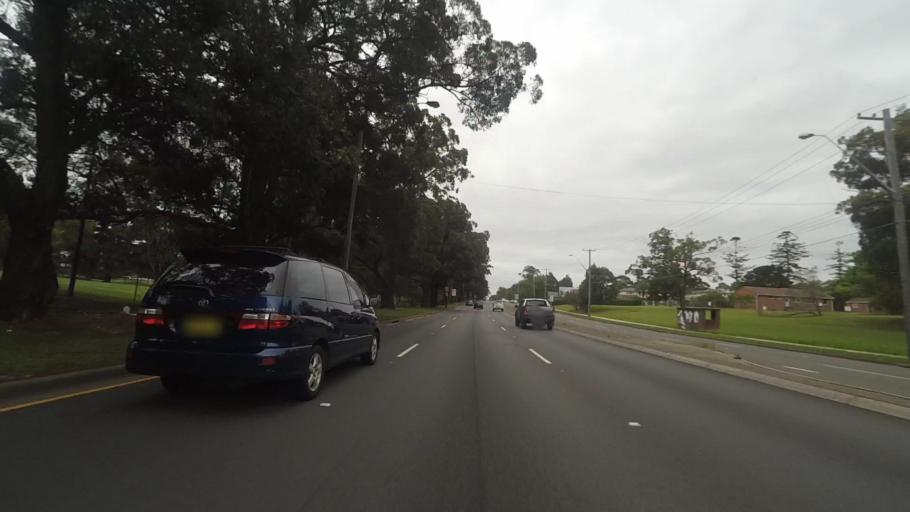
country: AU
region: New South Wales
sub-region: Auburn
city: Berala
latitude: -33.8832
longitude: 151.0402
